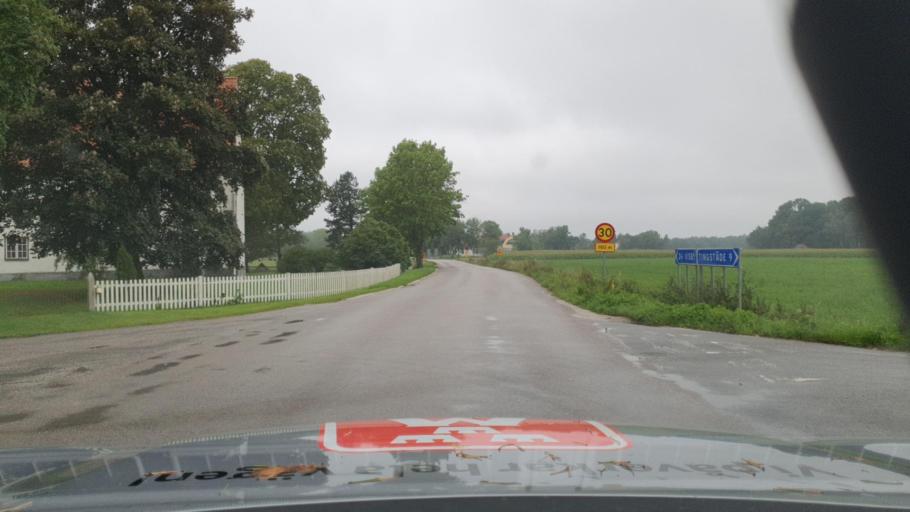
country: SE
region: Gotland
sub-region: Gotland
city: Visby
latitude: 57.7937
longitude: 18.5328
